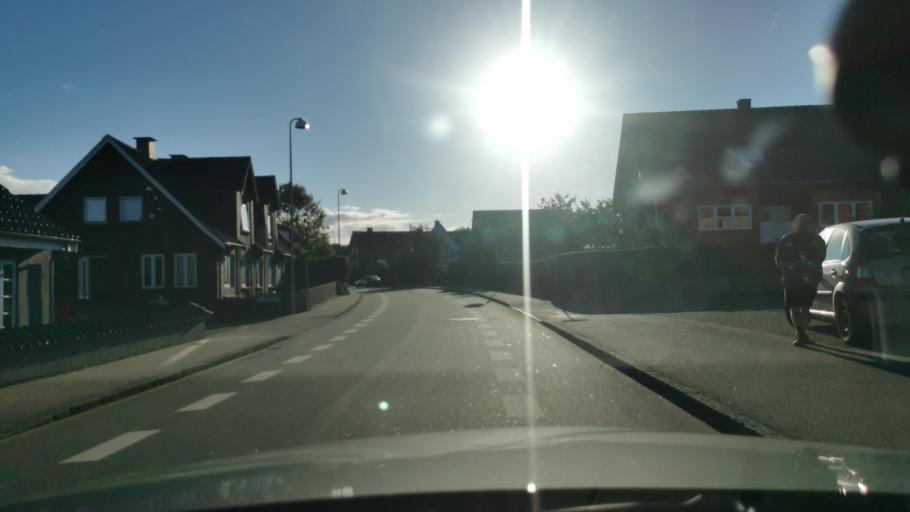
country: DK
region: Zealand
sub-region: Kalundborg Kommune
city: Svebolle
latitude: 55.6501
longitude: 11.2910
